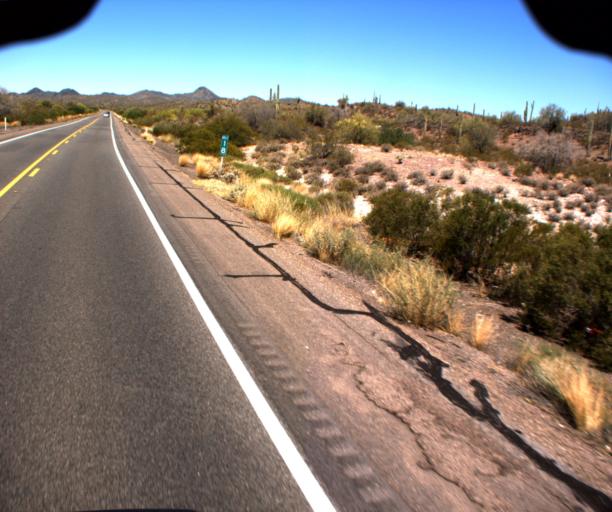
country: US
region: Arizona
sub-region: Maricopa County
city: Sun City West
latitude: 33.8346
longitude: -112.3304
